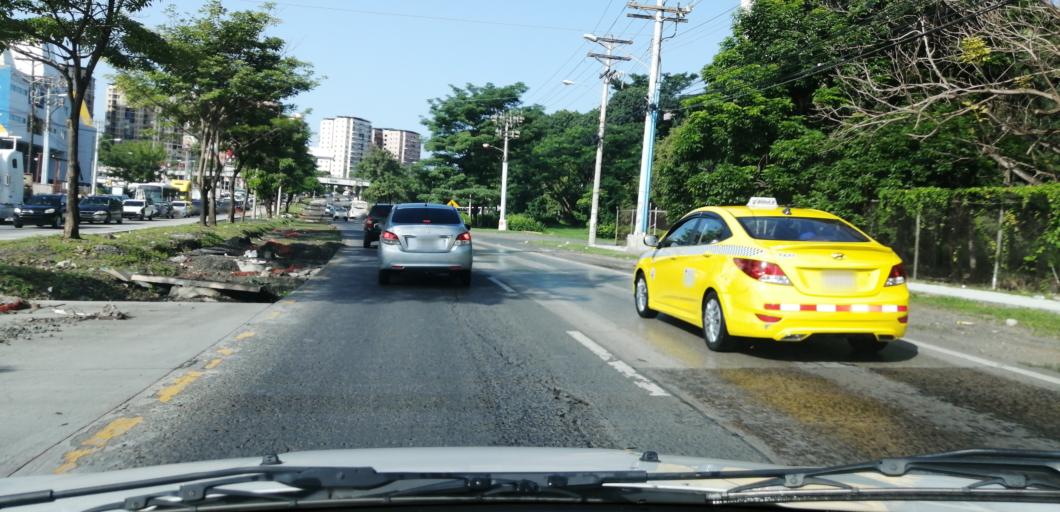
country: PA
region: Panama
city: Panama
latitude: 9.0298
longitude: -79.5191
